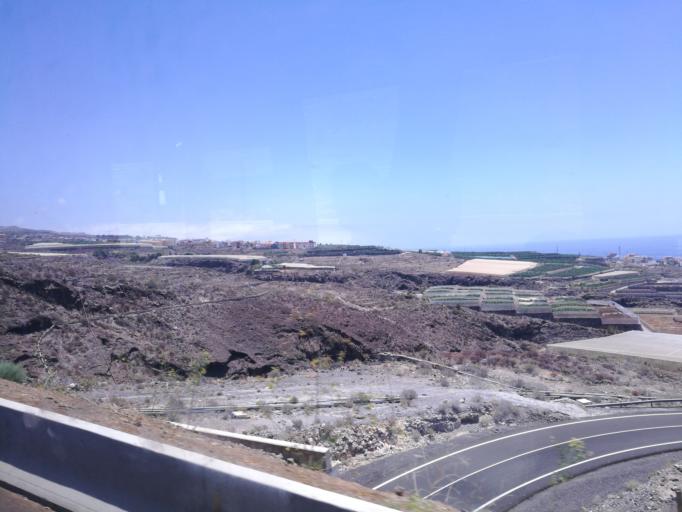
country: ES
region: Canary Islands
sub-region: Provincia de Santa Cruz de Tenerife
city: Guia de Isora
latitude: 28.1904
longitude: -16.7995
